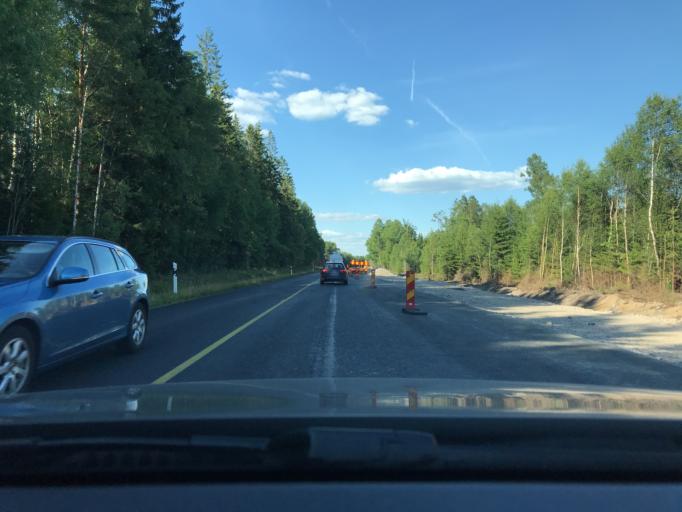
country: SE
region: Kronoberg
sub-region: Almhults Kommun
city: AElmhult
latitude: 56.6360
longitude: 14.2621
